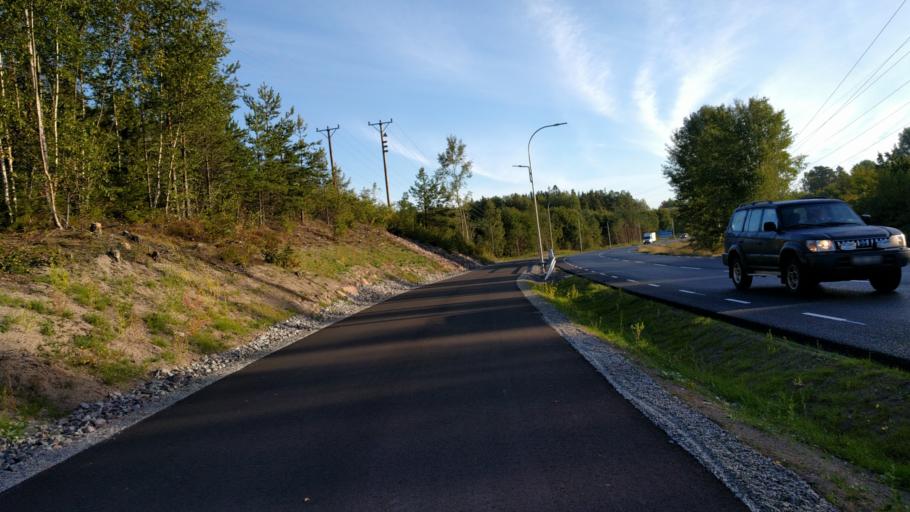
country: SE
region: Stockholm
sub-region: Taby Kommun
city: Taby
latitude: 59.4677
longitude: 18.0765
